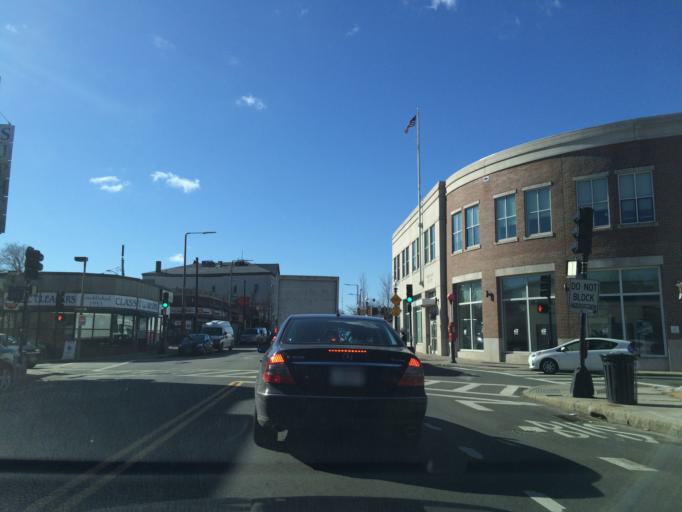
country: US
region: Massachusetts
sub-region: Suffolk County
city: Jamaica Plain
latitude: 42.3135
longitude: -71.1141
